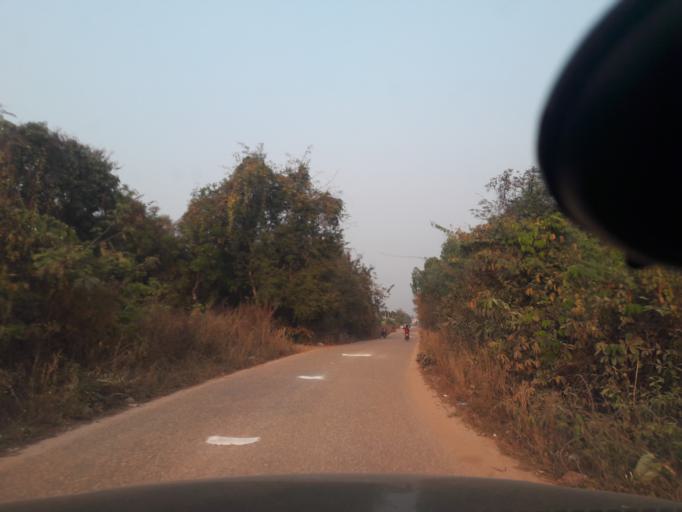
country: LA
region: Vientiane
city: Vientiane
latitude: 18.0632
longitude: 102.5285
